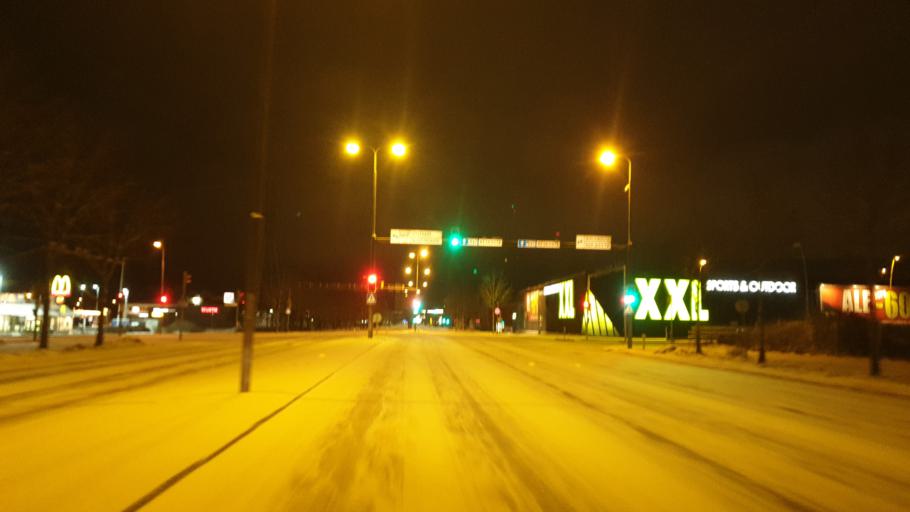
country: FI
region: Northern Ostrobothnia
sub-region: Oulu
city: Oulu
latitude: 64.9959
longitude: 25.4646
